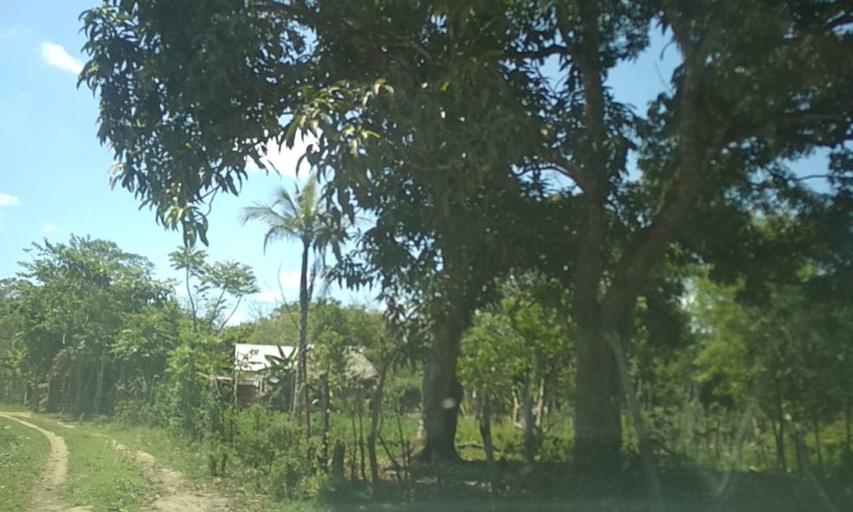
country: MX
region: Veracruz
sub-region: Moloacan
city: Cuichapa
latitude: 17.7861
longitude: -94.1936
